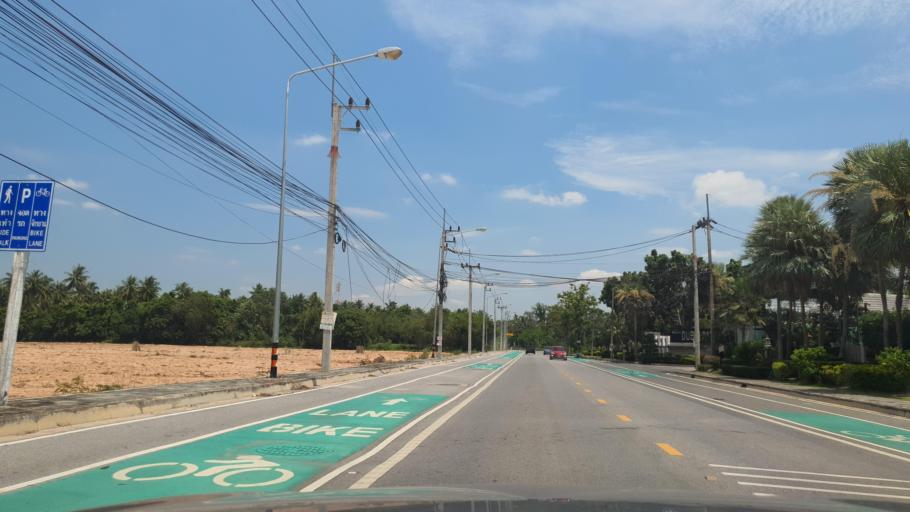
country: TH
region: Rayong
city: Ban Chang
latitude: 12.7982
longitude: 100.9475
